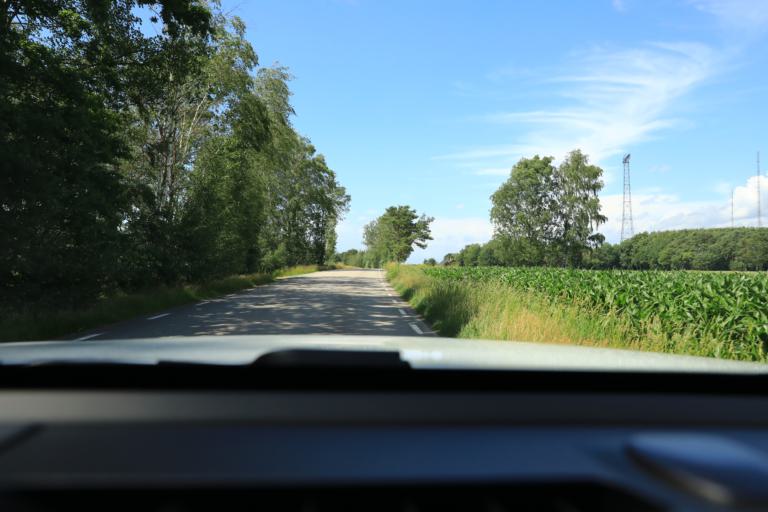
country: SE
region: Halland
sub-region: Varbergs Kommun
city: Tvaaker
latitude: 57.0964
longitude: 12.3880
